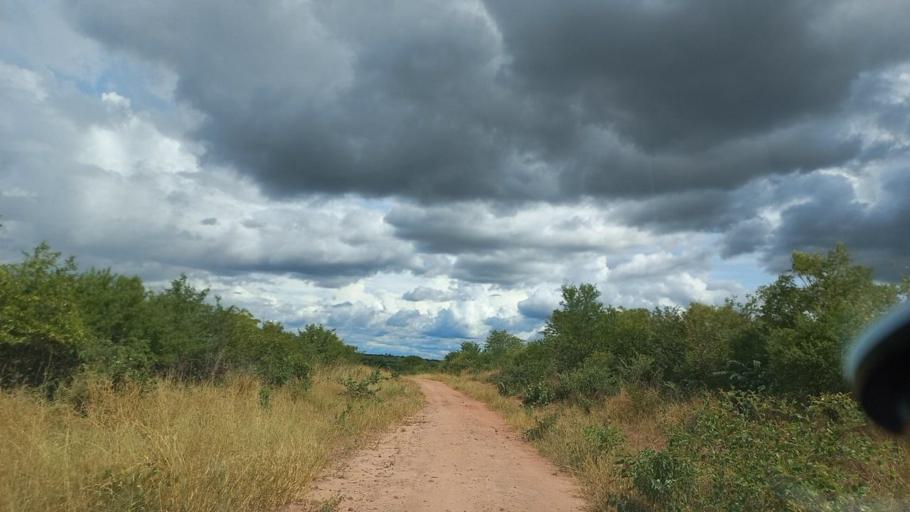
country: ZM
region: Lusaka
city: Luangwa
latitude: -15.6379
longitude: 30.3840
